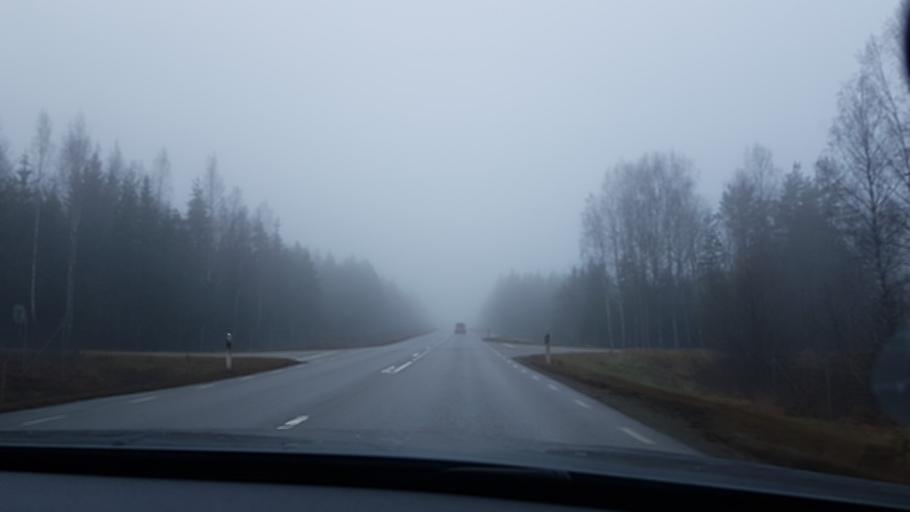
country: SE
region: Vaestra Goetaland
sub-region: Gullspangs Kommun
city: Gullspang
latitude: 58.9572
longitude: 14.0572
